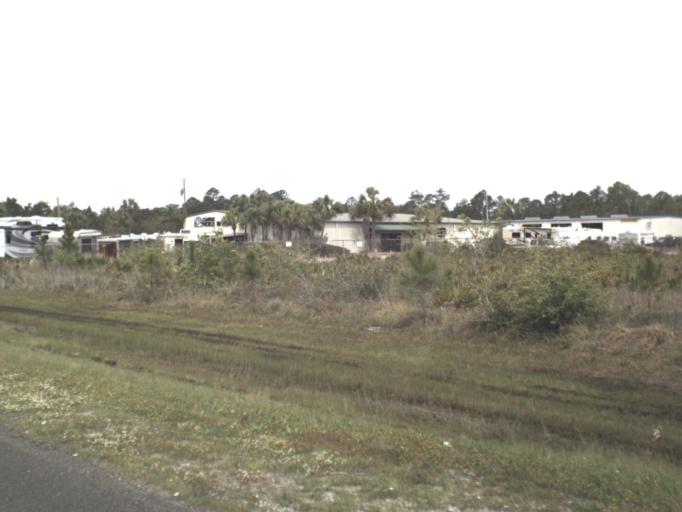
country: US
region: Florida
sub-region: Santa Rosa County
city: Woodlawn Beach
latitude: 30.4039
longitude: -86.9618
